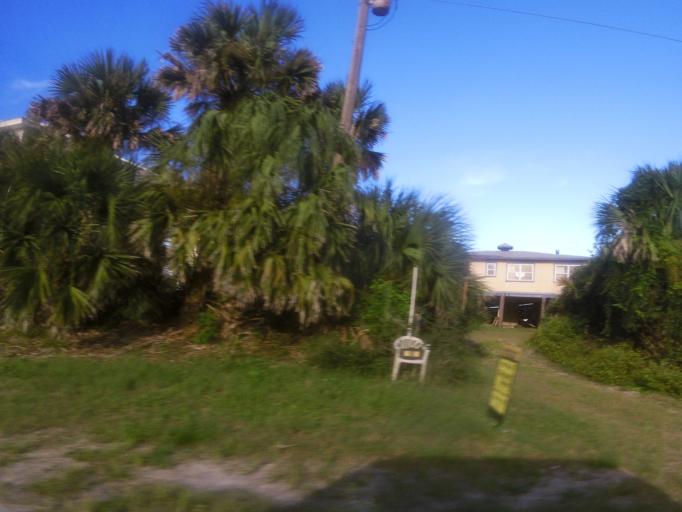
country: US
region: Florida
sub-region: Flagler County
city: Flagler Beach
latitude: 29.5353
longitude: -81.1548
